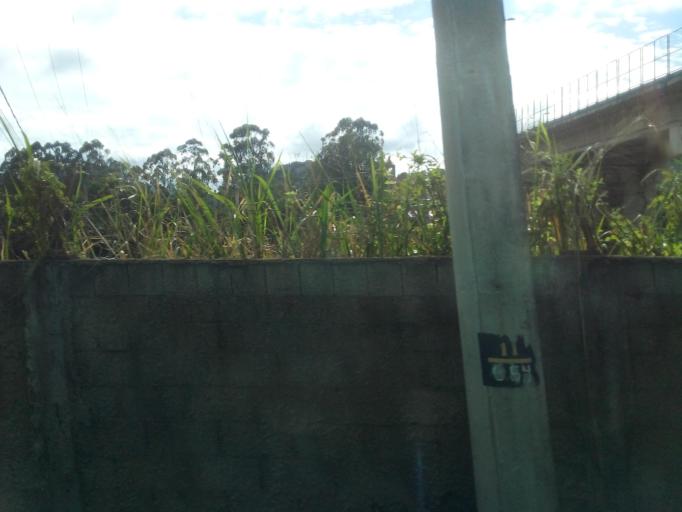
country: BR
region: Minas Gerais
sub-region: Belo Horizonte
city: Belo Horizonte
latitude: -19.8784
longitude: -43.8604
